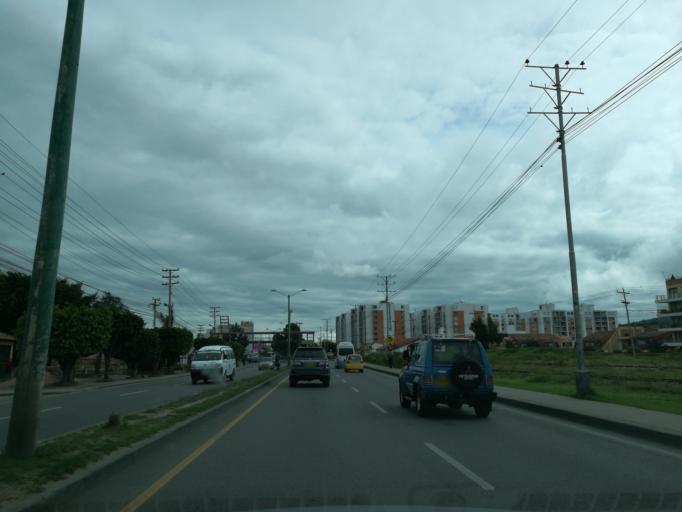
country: CO
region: Boyaca
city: Tunja
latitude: 5.5504
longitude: -73.3531
